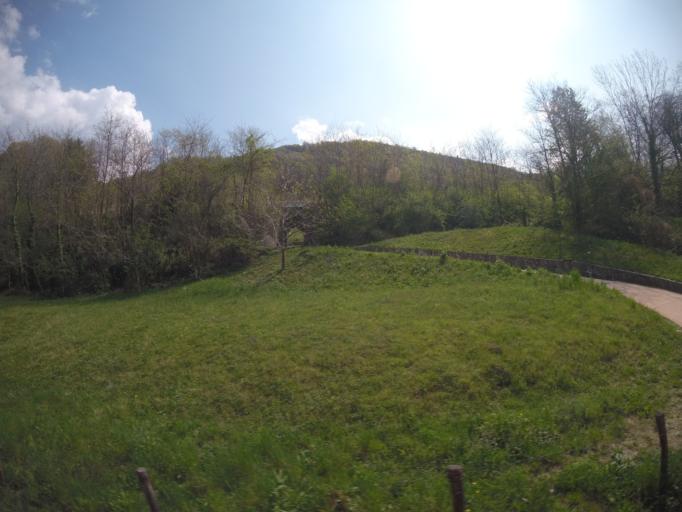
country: IT
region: Piedmont
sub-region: Provincia di Novara
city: Pettenasco
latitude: 45.8363
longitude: 8.3998
